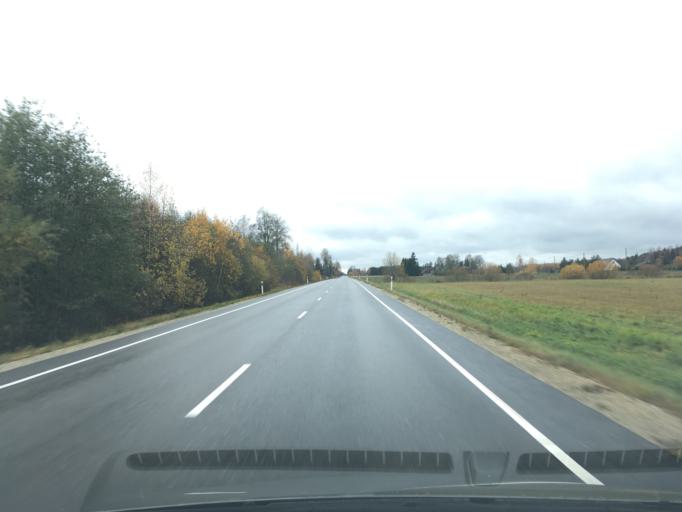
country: EE
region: Jogevamaa
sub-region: Tabivere vald
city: Tabivere
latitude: 58.4524
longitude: 26.5244
